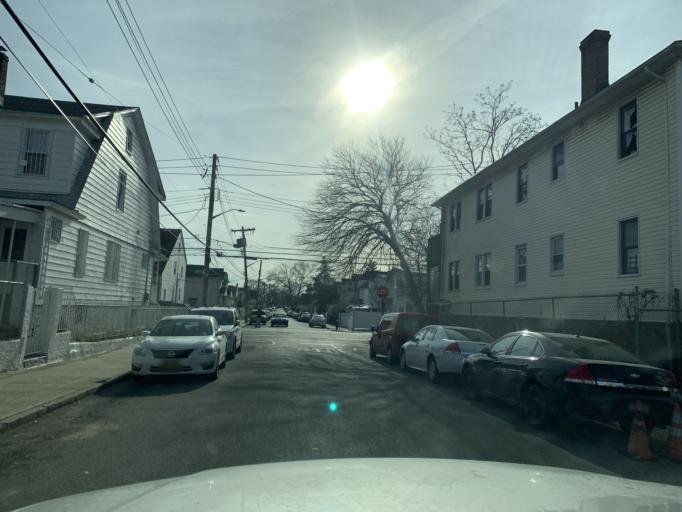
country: US
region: New York
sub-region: Queens County
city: Jamaica
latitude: 40.6957
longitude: -73.7895
